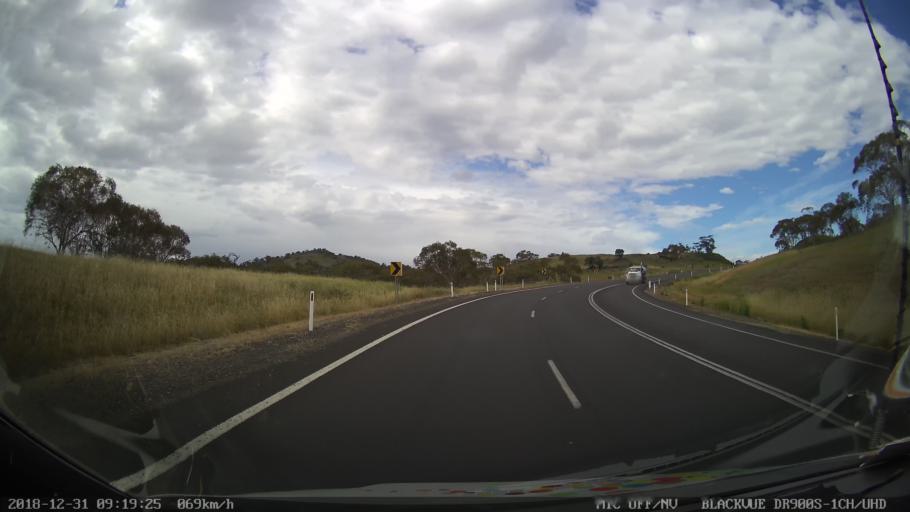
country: AU
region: New South Wales
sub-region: Snowy River
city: Jindabyne
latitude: -36.4152
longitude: 148.5861
